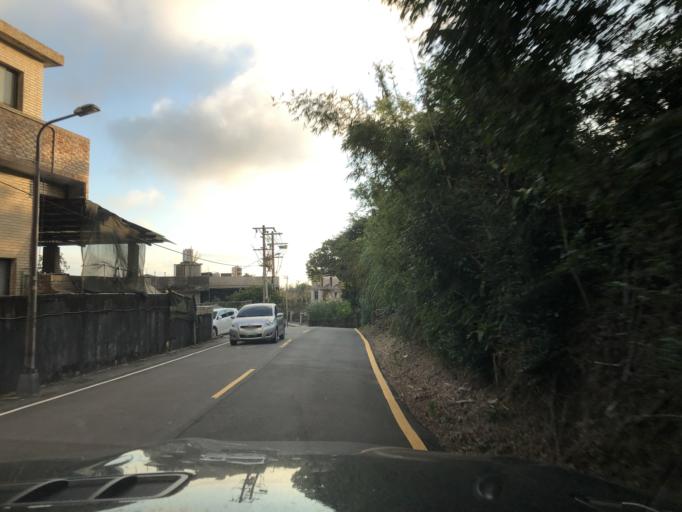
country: TW
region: Taipei
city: Taipei
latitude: 25.1482
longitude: 121.5590
